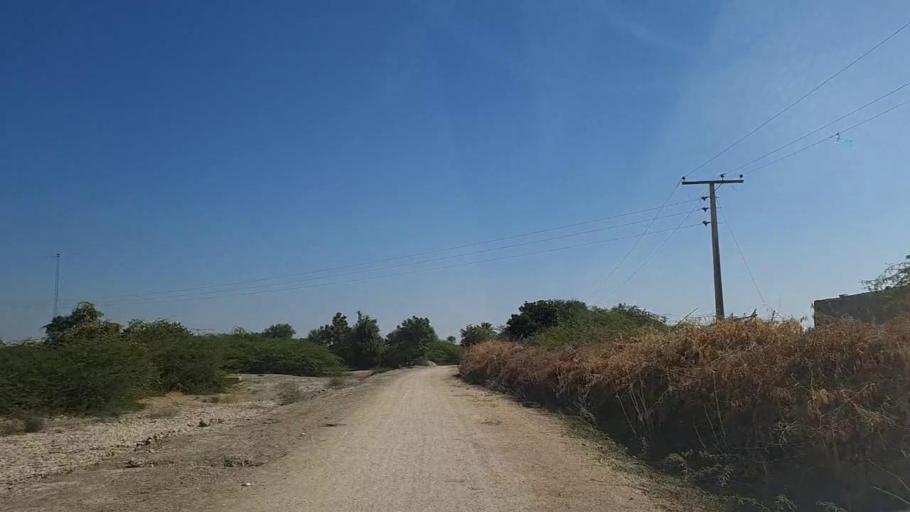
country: PK
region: Sindh
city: Samaro
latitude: 25.3649
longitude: 69.4939
